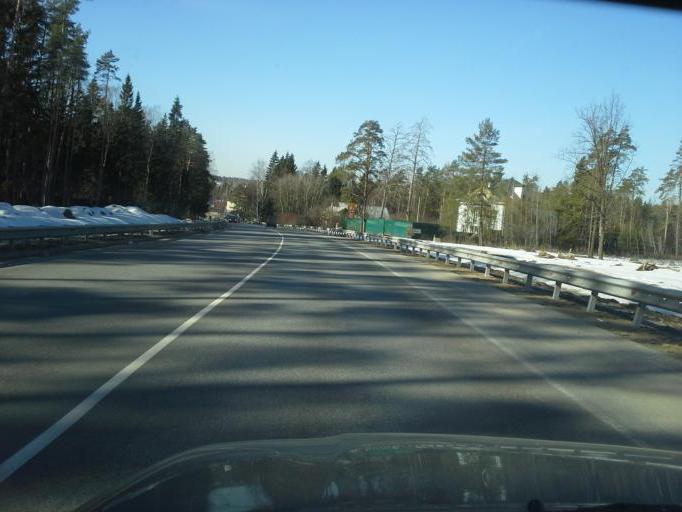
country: RU
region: Moskovskaya
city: Gorki Vtoryye
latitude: 55.6794
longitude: 37.1623
